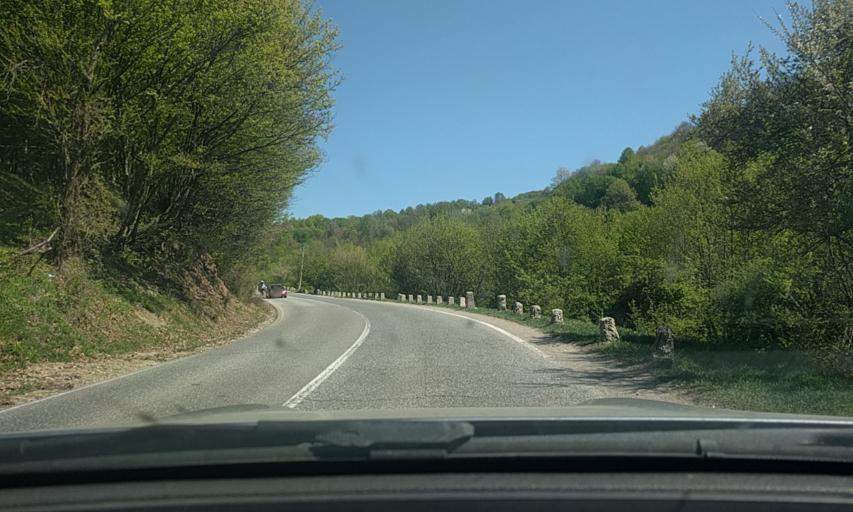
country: RO
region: Brasov
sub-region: Comuna Vama Buzaului
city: Acris
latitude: 45.6776
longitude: 25.9438
